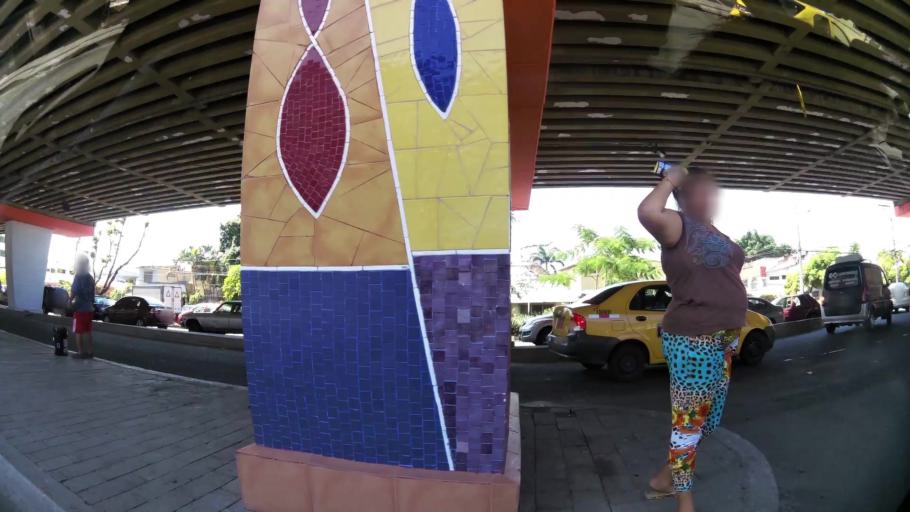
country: EC
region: Guayas
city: Guayaquil
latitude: -2.1674
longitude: -79.9213
